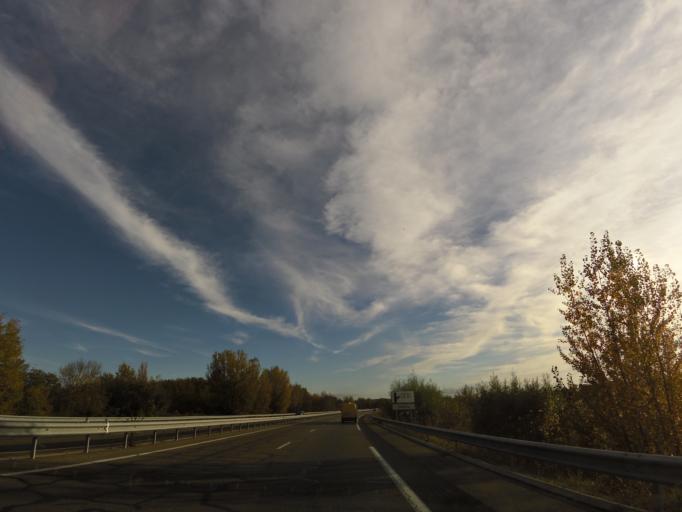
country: FR
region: Languedoc-Roussillon
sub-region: Departement du Gard
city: Saint-Hilaire-de-Brethmas
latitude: 44.0816
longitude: 4.1110
